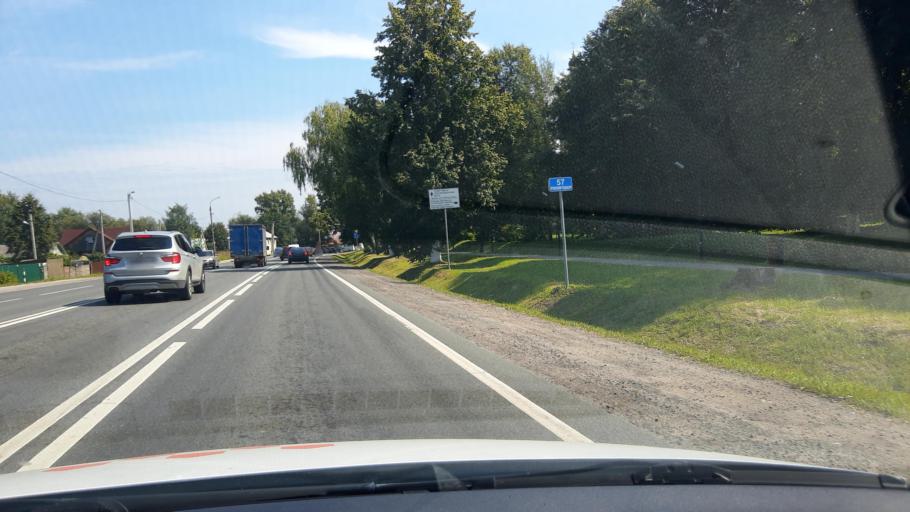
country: RU
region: Moskovskaya
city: Bronnitsy
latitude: 55.4301
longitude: 38.2523
